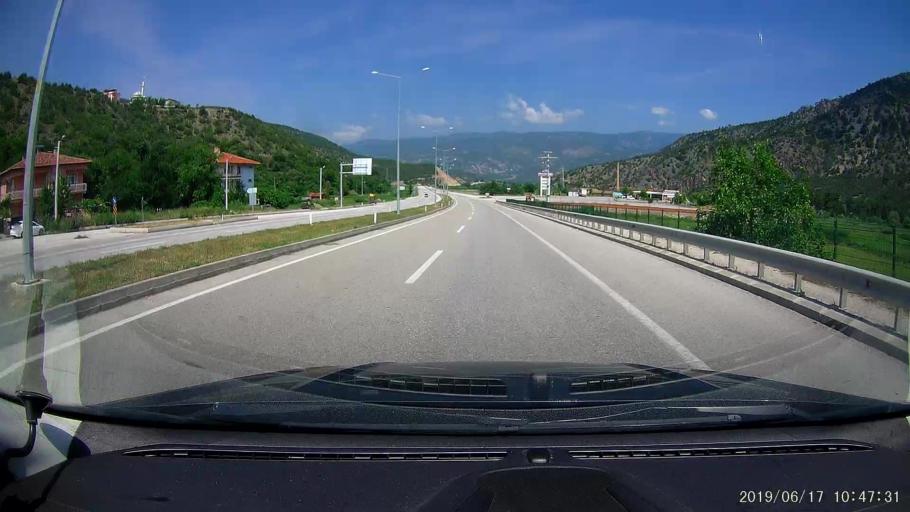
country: TR
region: Corum
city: Hacihamza
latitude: 41.0779
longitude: 34.4479
